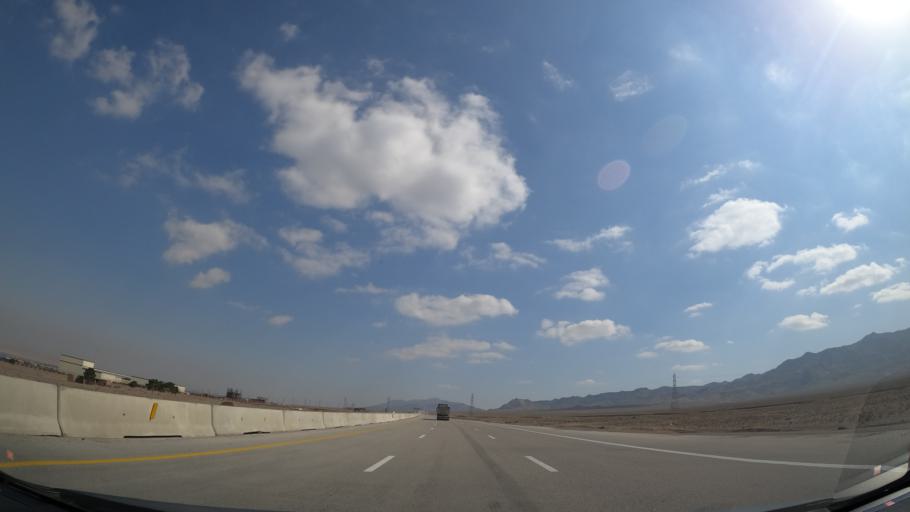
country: IR
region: Alborz
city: Eshtehard
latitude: 35.7179
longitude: 50.5742
